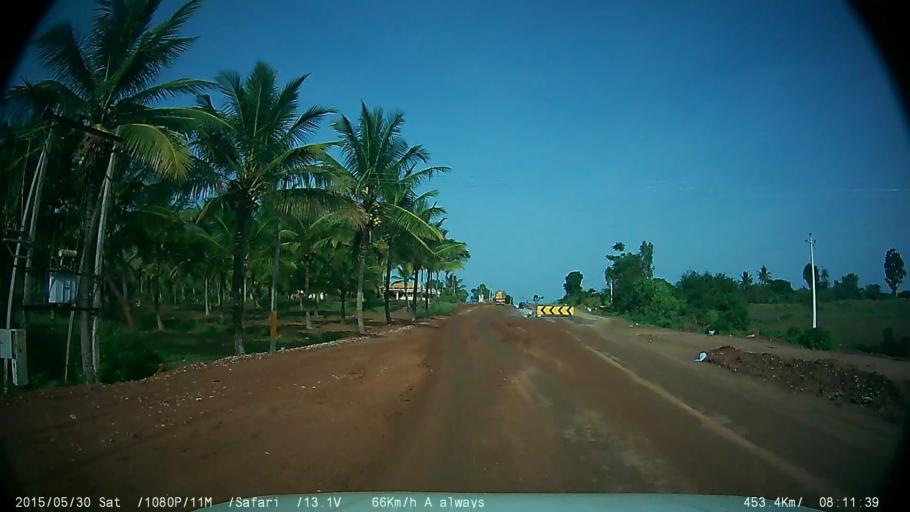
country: IN
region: Karnataka
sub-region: Chamrajnagar
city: Gundlupet
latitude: 11.7793
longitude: 76.5887
